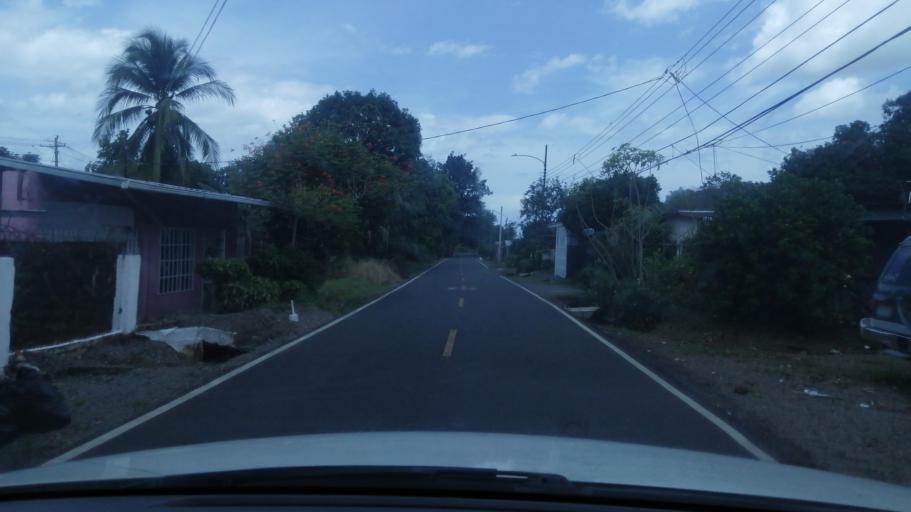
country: PA
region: Chiriqui
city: David
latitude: 8.4135
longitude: -82.4271
